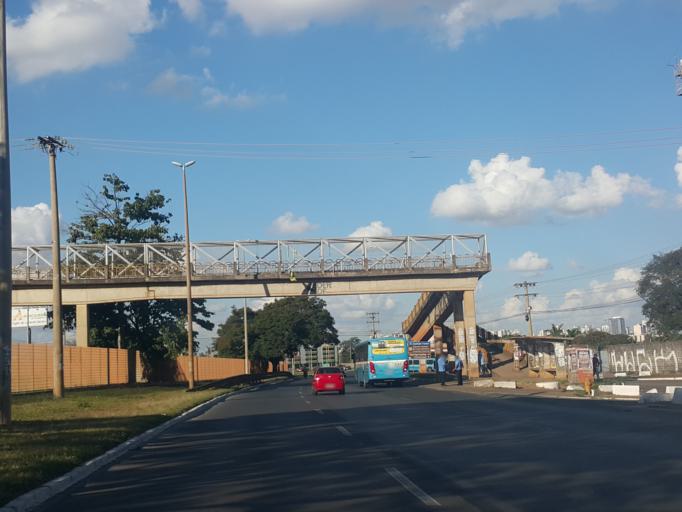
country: BR
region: Federal District
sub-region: Brasilia
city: Brasilia
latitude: -15.8349
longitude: -48.0817
